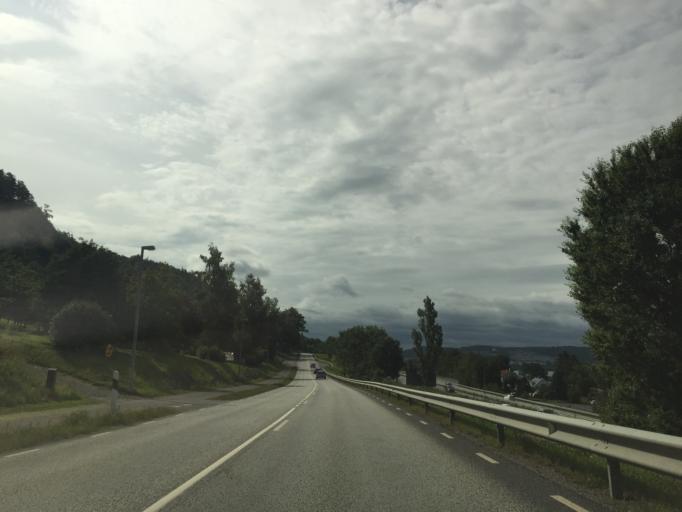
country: SE
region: Joenkoeping
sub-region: Jonkopings Kommun
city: Huskvarna
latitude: 57.8231
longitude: 14.2708
